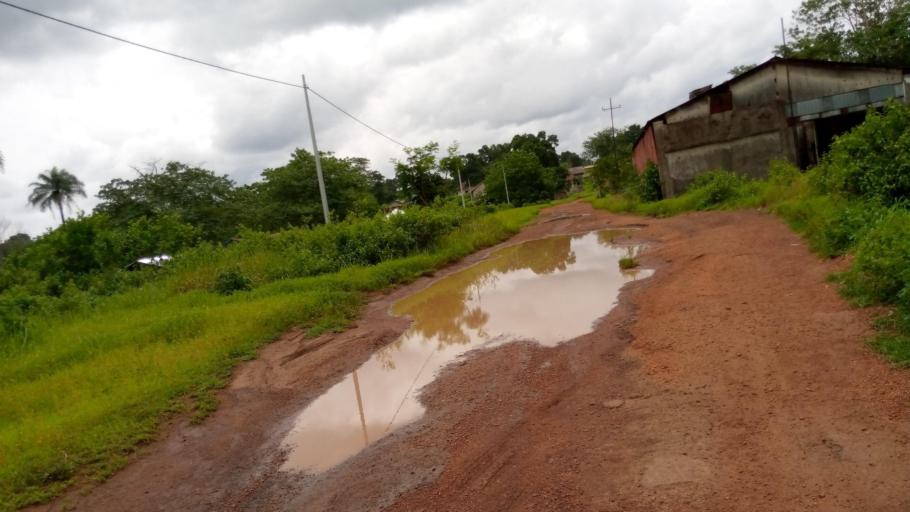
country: SL
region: Southern Province
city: Rotifunk
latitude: 8.1908
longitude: -12.5697
